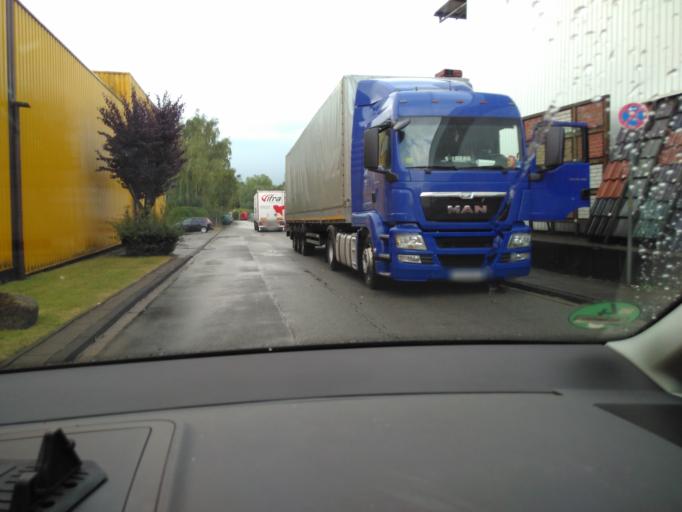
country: DE
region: North Rhine-Westphalia
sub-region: Regierungsbezirk Detmold
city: Bielefeld
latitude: 52.0384
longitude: 8.5962
